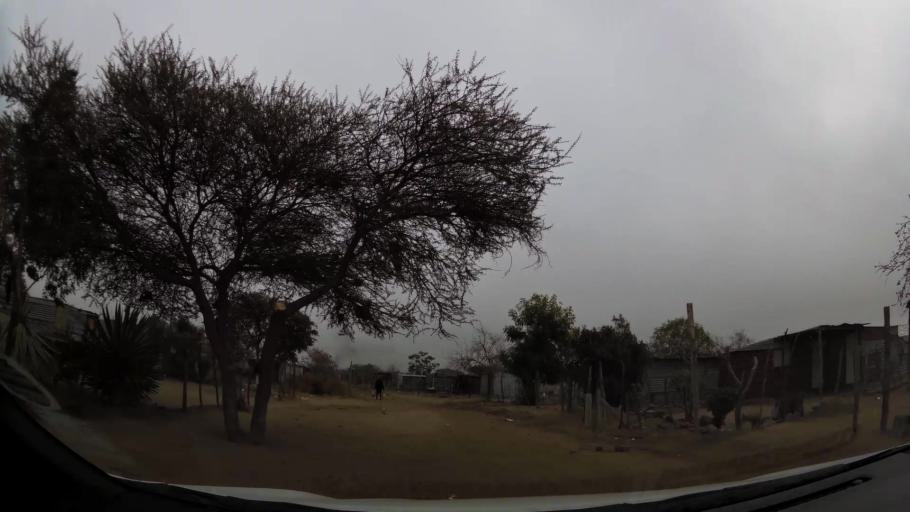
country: ZA
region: Limpopo
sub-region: Capricorn District Municipality
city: Polokwane
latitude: -23.8320
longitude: 29.3858
